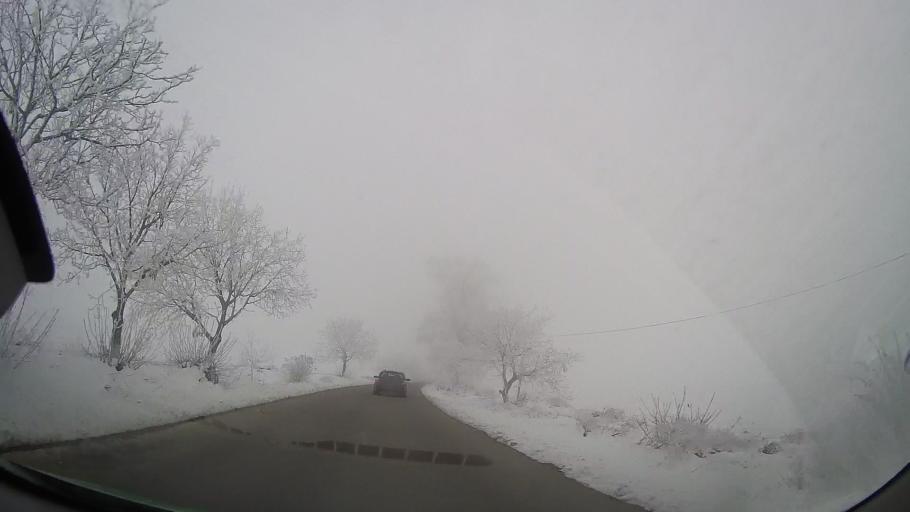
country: RO
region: Neamt
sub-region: Comuna Sabaoani
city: Sabaoani
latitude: 46.9898
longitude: 26.8629
